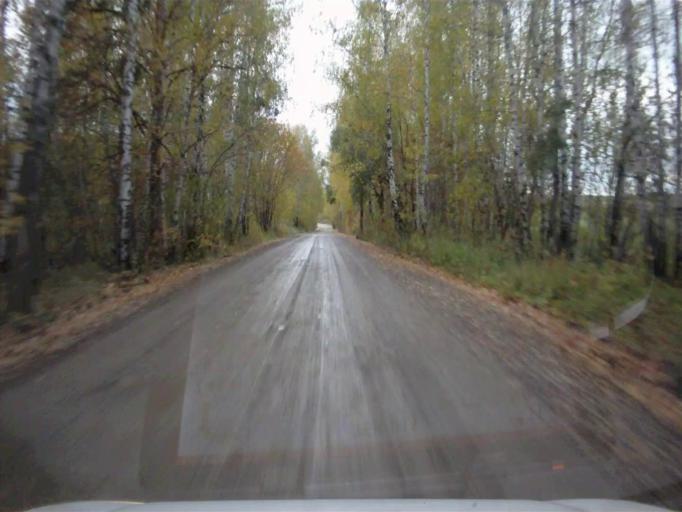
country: RU
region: Sverdlovsk
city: Mikhaylovsk
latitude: 56.1722
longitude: 59.2200
